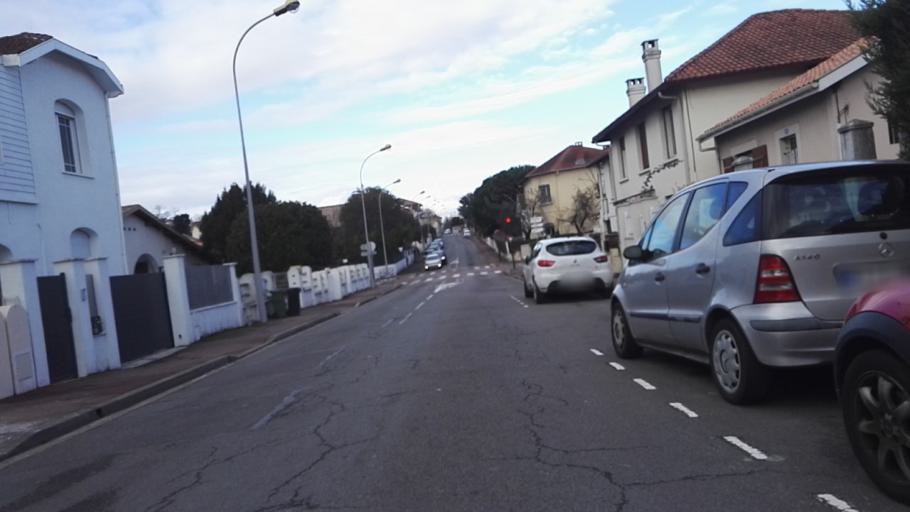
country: FR
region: Aquitaine
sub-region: Departement de la Gironde
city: Talence
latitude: 44.8081
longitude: -0.5862
